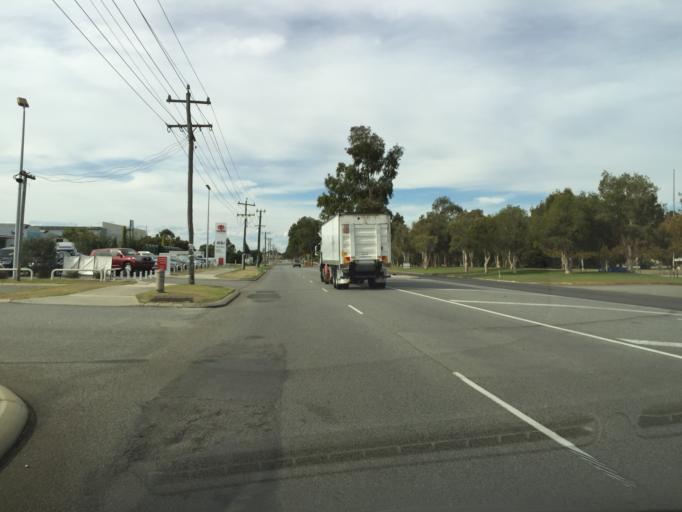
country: AU
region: Western Australia
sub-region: Canning
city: Willetton
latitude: -32.0657
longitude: 115.9003
